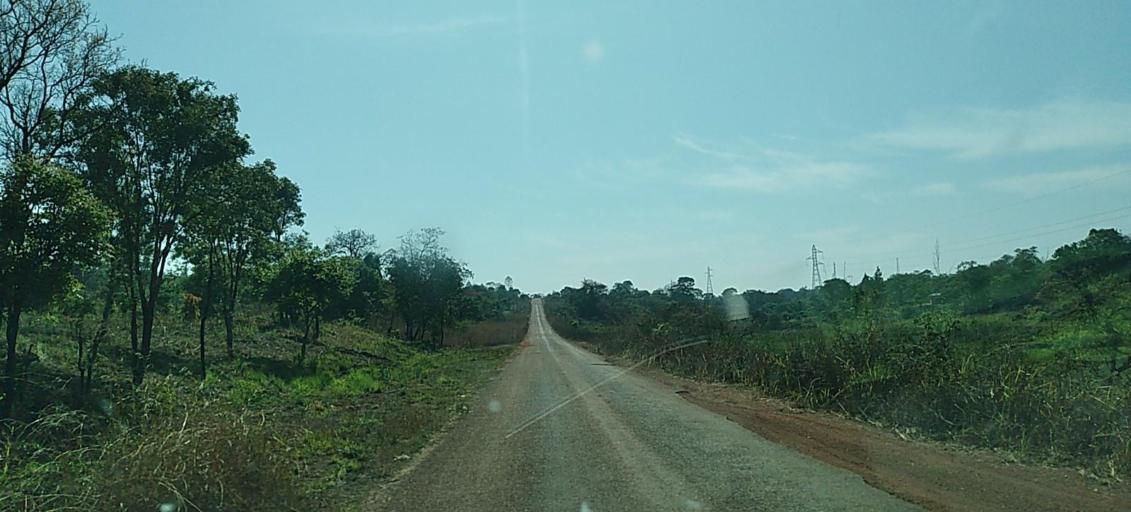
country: ZM
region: North-Western
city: Mwinilunga
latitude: -11.8258
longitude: 25.1292
